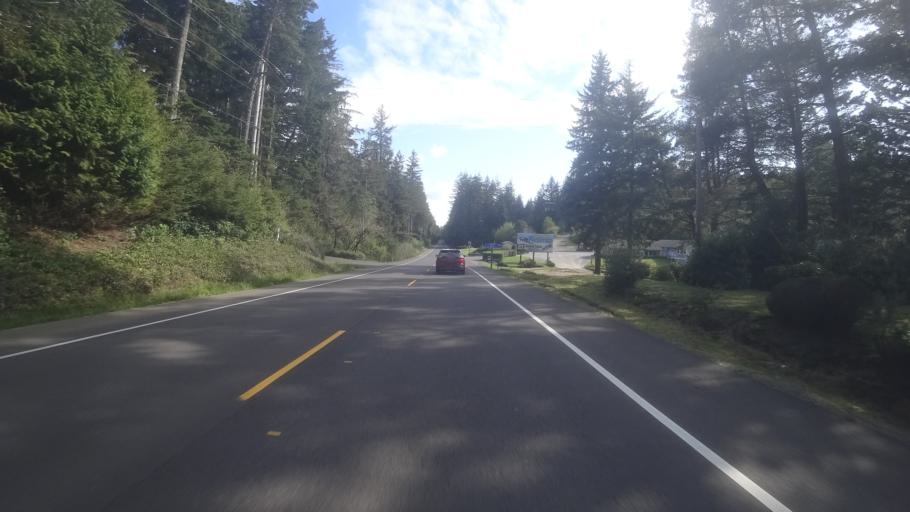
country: US
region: Oregon
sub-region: Lane County
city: Dunes City
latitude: 43.9150
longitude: -124.1105
